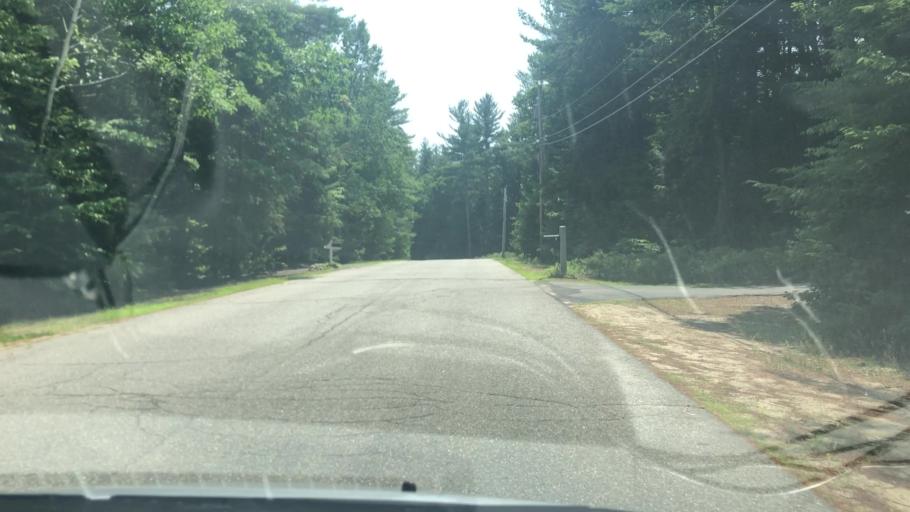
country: US
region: New Hampshire
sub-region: Hillsborough County
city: Milford
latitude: 42.8780
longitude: -71.6158
